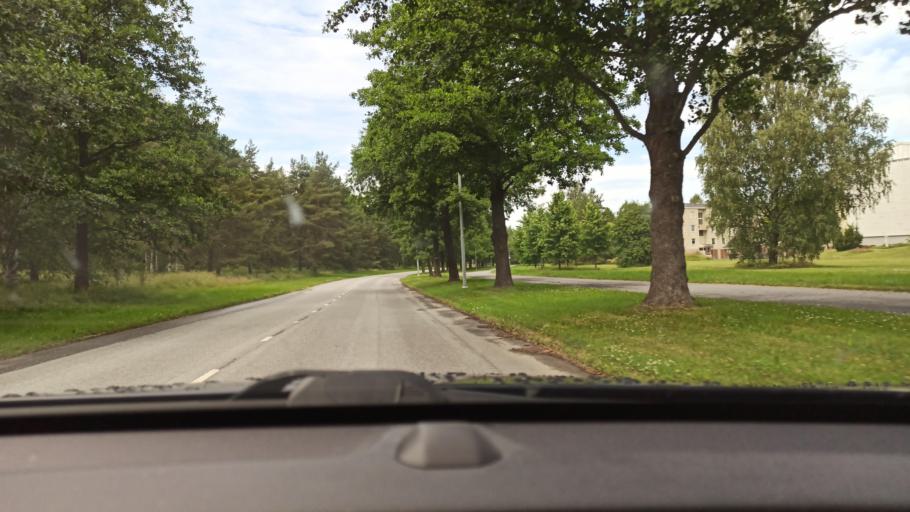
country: FI
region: Satakunta
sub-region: Pori
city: Pori
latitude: 61.5052
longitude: 21.7786
